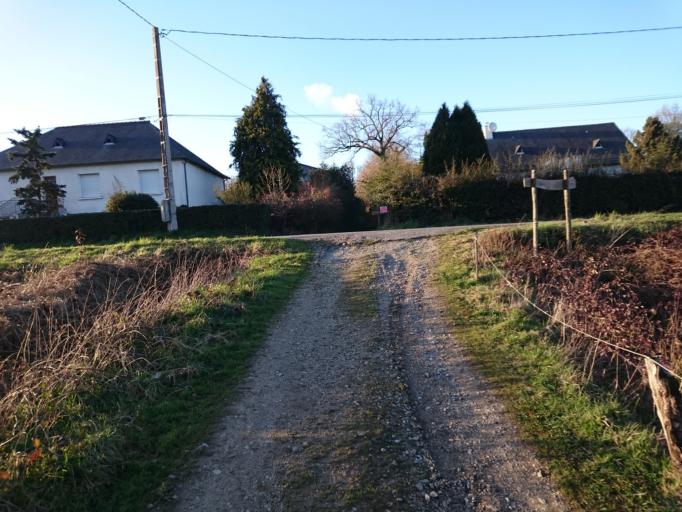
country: FR
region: Brittany
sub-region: Departement d'Ille-et-Vilaine
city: Chanteloup
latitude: 47.9352
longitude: -1.6090
